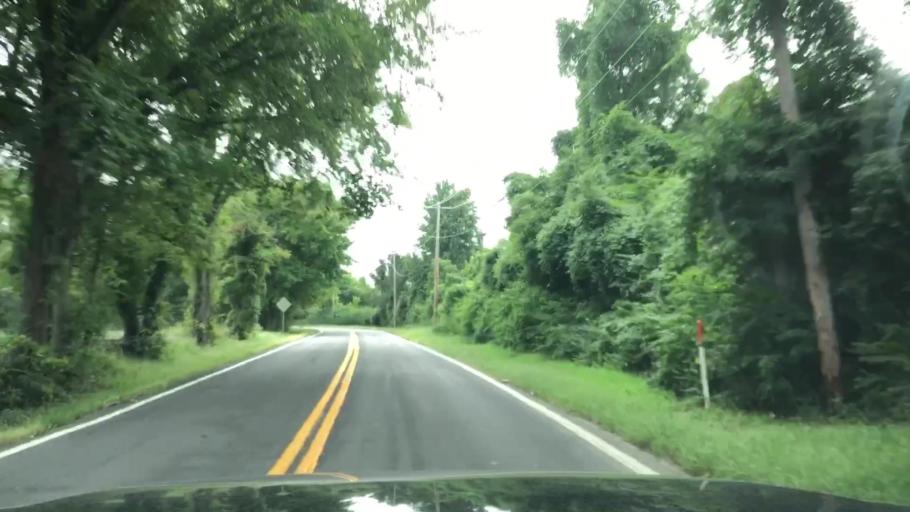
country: US
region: Missouri
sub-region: Saint Louis County
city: Hazelwood
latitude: 38.8147
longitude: -90.3777
